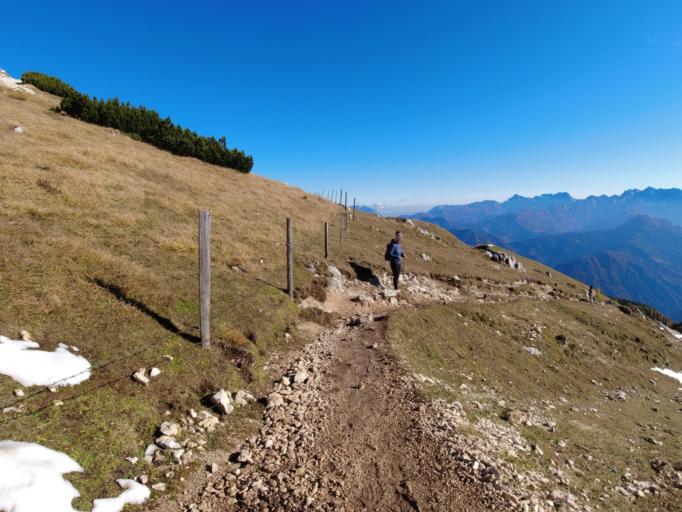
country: AT
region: Carinthia
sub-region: Politischer Bezirk Volkermarkt
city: Gallizien
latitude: 46.5045
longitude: 14.4860
